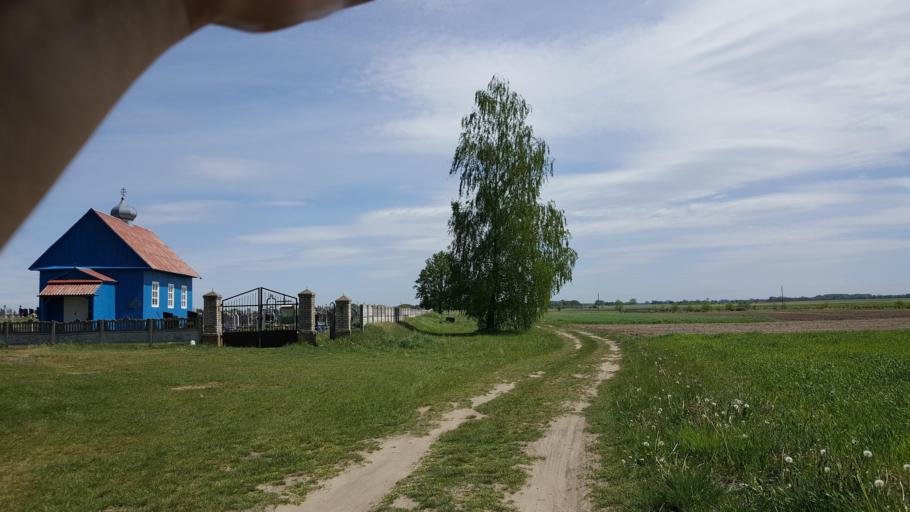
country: BY
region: Brest
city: Kobryn
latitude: 52.3350
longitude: 24.2629
